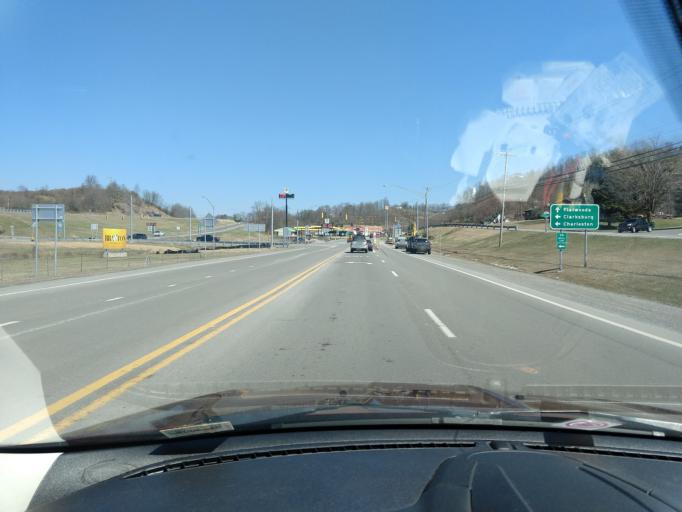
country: US
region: West Virginia
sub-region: Braxton County
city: Sutton
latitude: 38.7015
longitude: -80.6627
